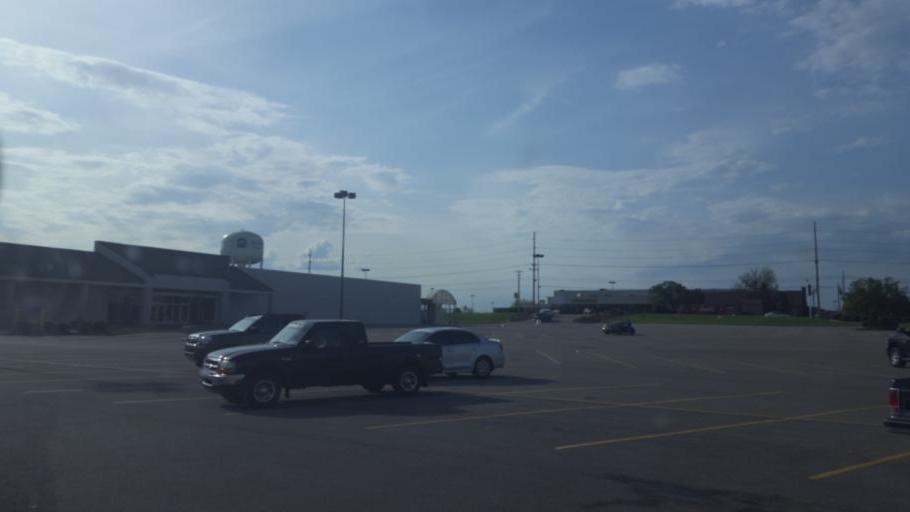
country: US
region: Kentucky
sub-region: Warren County
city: Bowling Green
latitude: 36.9440
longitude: -86.4247
